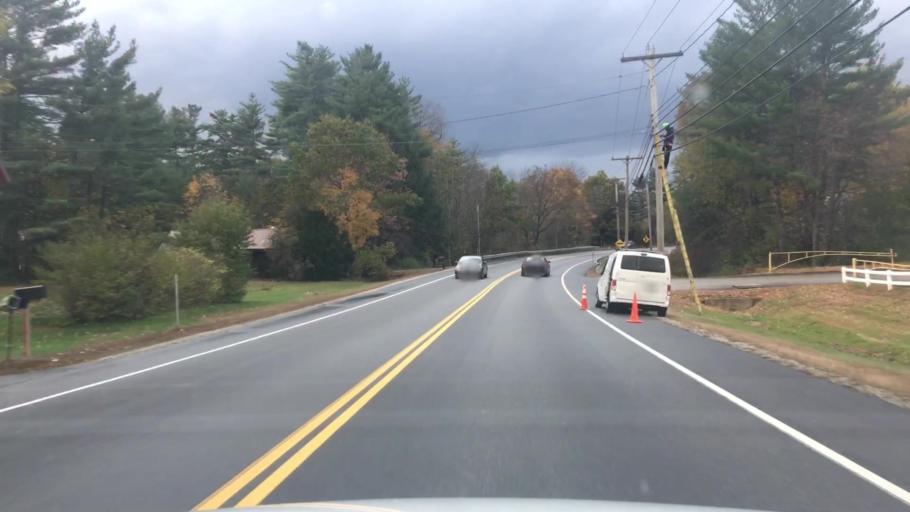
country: US
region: New Hampshire
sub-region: Merrimack County
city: Epsom
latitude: 43.2234
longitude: -71.3387
